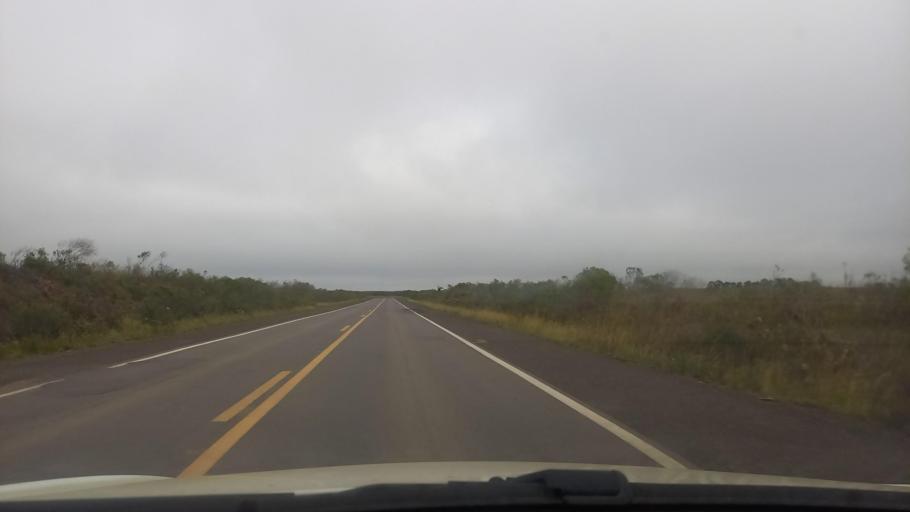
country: BR
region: Rio Grande do Sul
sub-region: Cacequi
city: Cacequi
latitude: -30.0676
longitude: -54.6129
